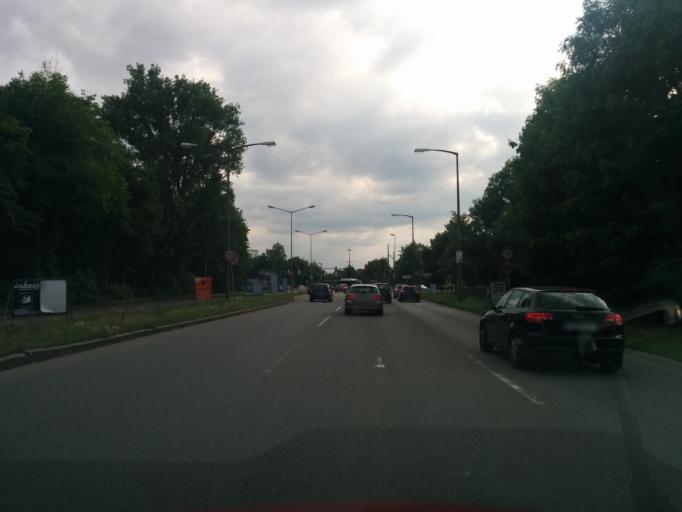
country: DE
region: Bavaria
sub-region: Swabia
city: Augsburg
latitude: 48.3949
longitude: 10.9168
